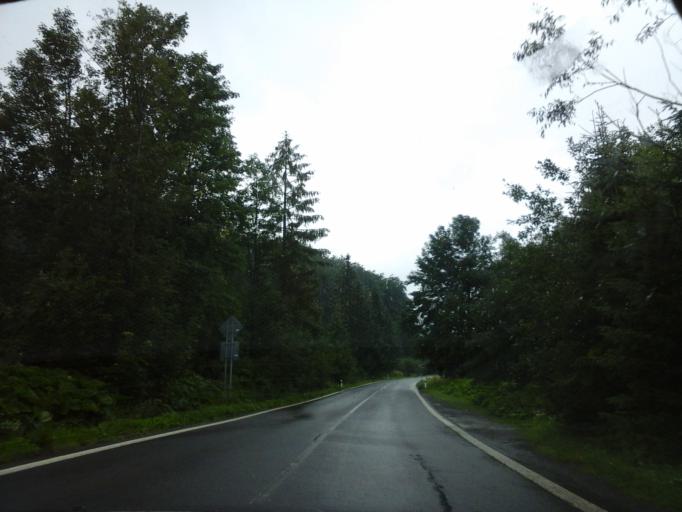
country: PL
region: Lesser Poland Voivodeship
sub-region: Powiat tatrzanski
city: Bukowina Tatrzanska
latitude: 49.2657
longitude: 20.1407
